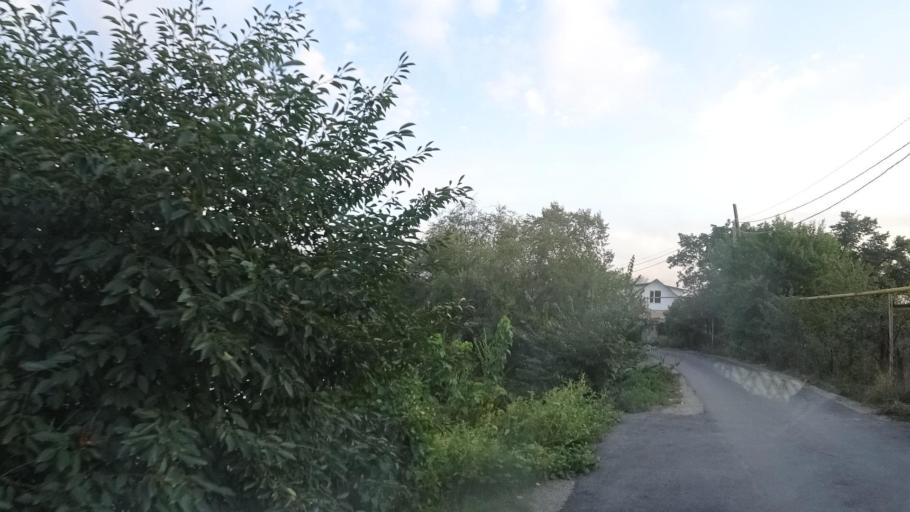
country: KZ
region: Almaty Oblysy
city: Pervomayskiy
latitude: 43.3383
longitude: 76.9977
